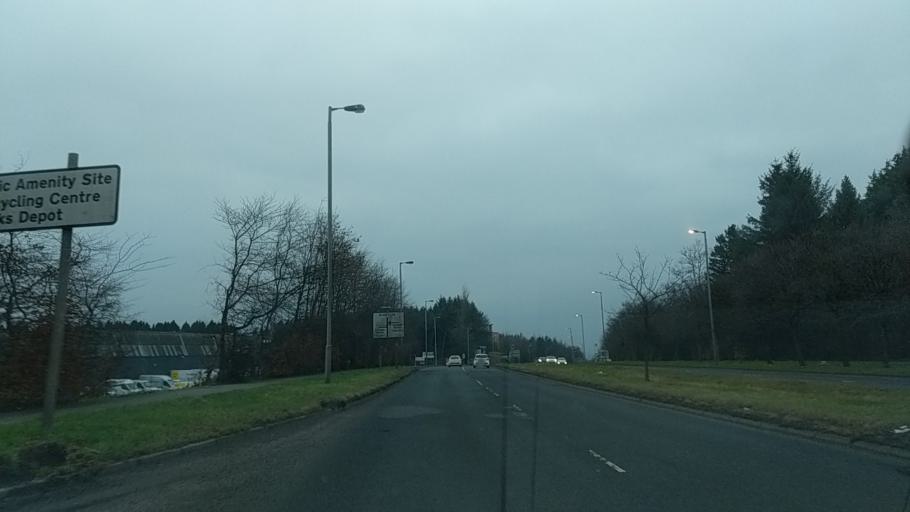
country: GB
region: Scotland
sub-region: Glasgow City
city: Carmunnock
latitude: 55.7664
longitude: -4.2161
